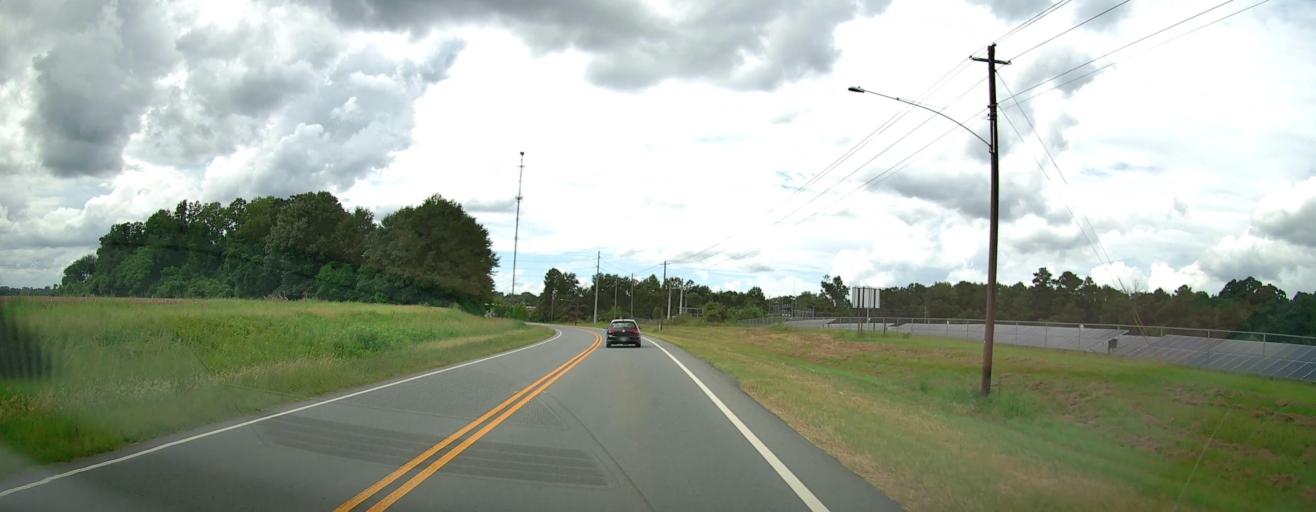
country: US
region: Georgia
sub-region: Macon County
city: Oglethorpe
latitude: 32.2927
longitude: -84.0493
